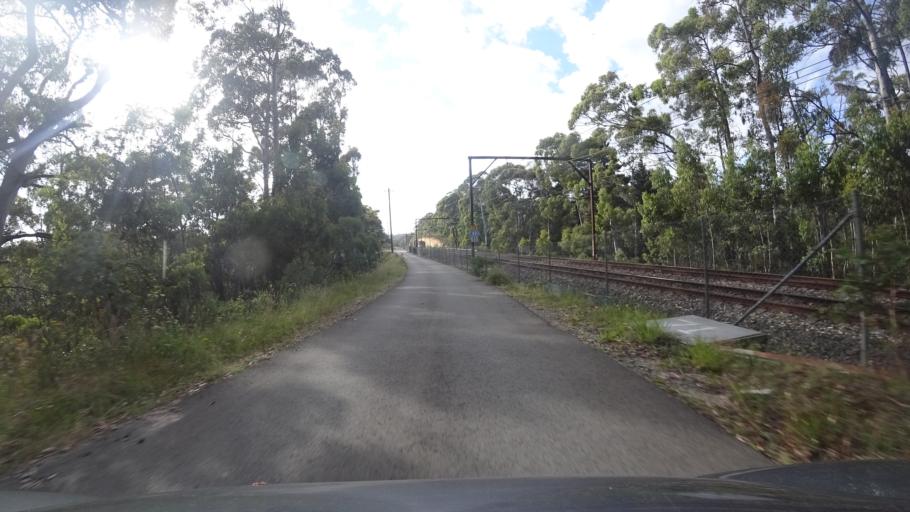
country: AU
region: New South Wales
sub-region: Lithgow
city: Lithgow
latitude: -33.4742
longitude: 150.2414
